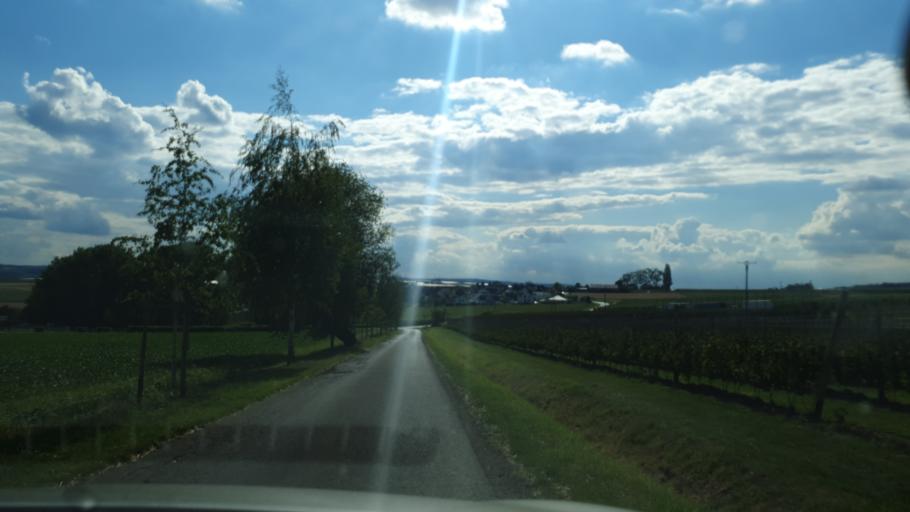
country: DE
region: Rheinland-Pfalz
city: Unkel
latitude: 50.5946
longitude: 7.1541
